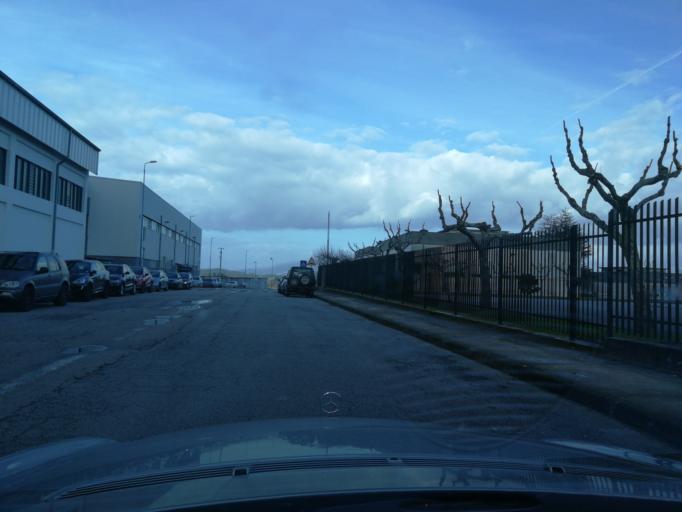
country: PT
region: Viana do Castelo
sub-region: Valenca
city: Valenca
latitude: 42.0295
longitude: -8.6395
